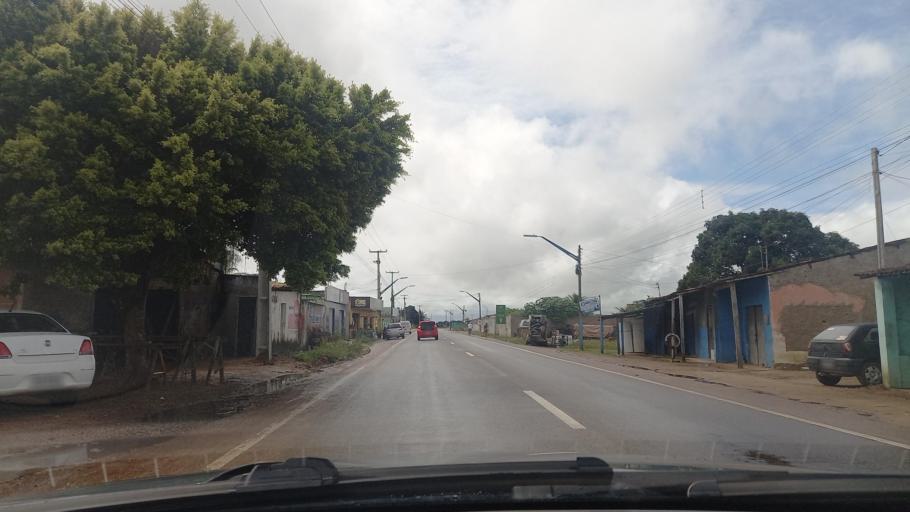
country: BR
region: Alagoas
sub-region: Limoeiro De Anadia
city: Limoeiro de Anadia
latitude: -9.7582
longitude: -36.5562
